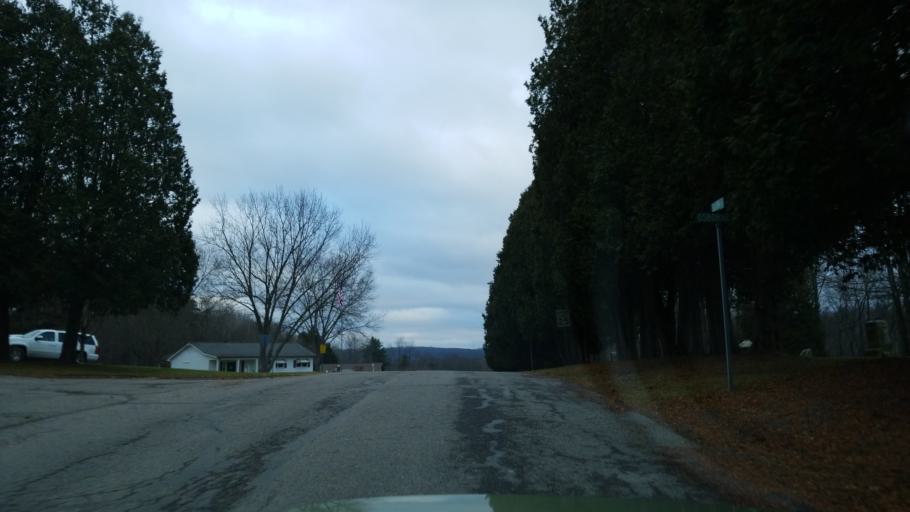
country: US
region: Pennsylvania
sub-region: Jefferson County
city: Falls Creek
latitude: 41.1414
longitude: -78.8106
